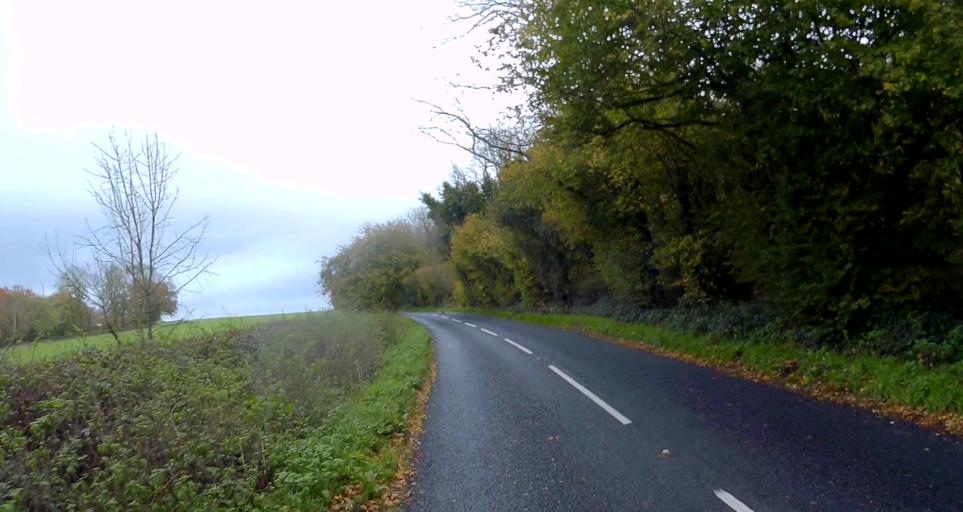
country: GB
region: England
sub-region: Hampshire
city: Four Marks
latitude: 51.1230
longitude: -1.1744
